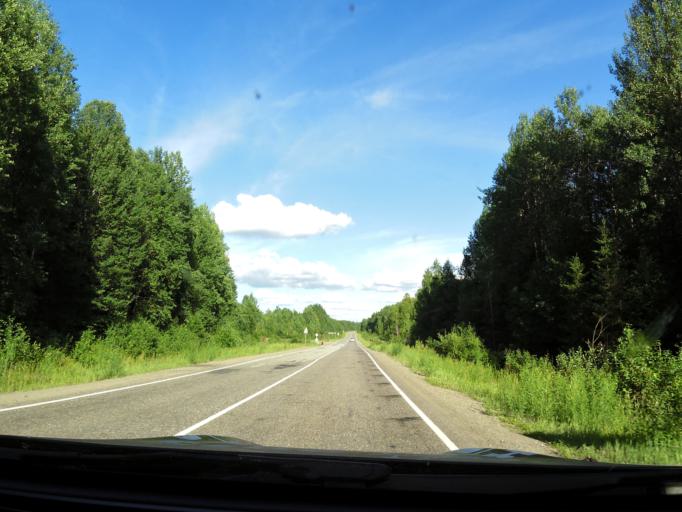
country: RU
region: Kirov
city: Omutninsk
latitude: 58.7564
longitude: 52.0329
